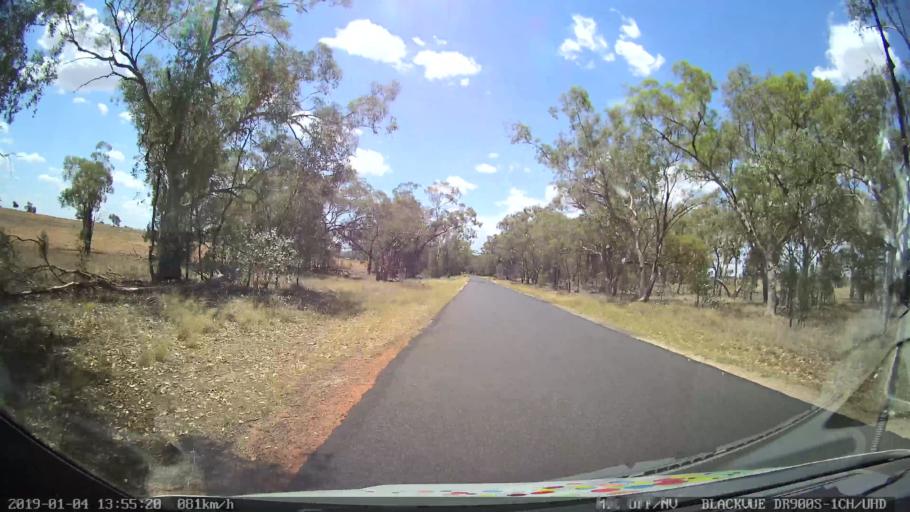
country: AU
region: New South Wales
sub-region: Dubbo Municipality
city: Dubbo
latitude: -32.3631
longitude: 148.5864
